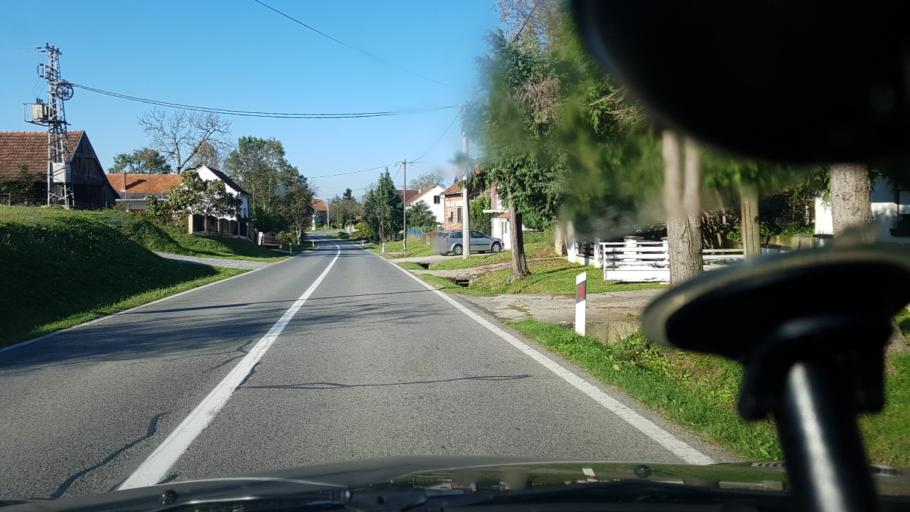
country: HR
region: Bjelovarsko-Bilogorska
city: Gudovac
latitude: 45.8068
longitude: 16.7173
